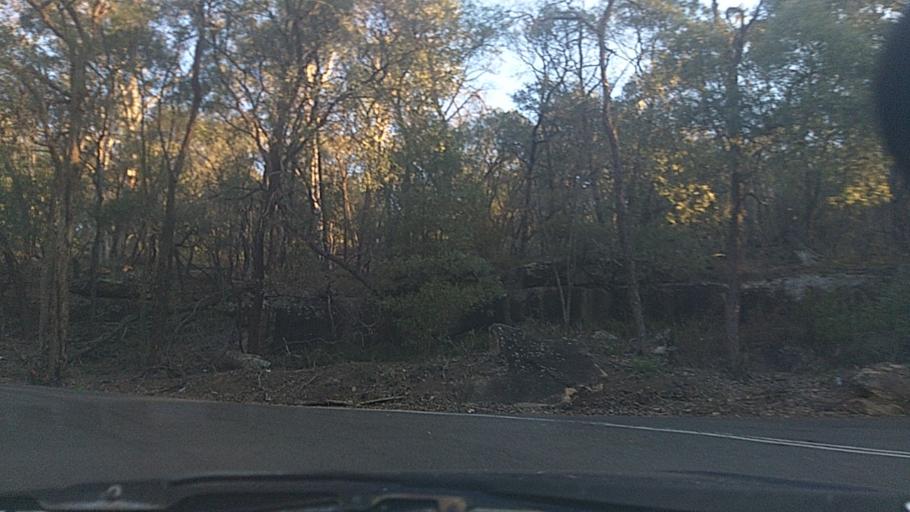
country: AU
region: New South Wales
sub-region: Wollondilly
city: Douglas Park
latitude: -34.1923
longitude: 150.7101
